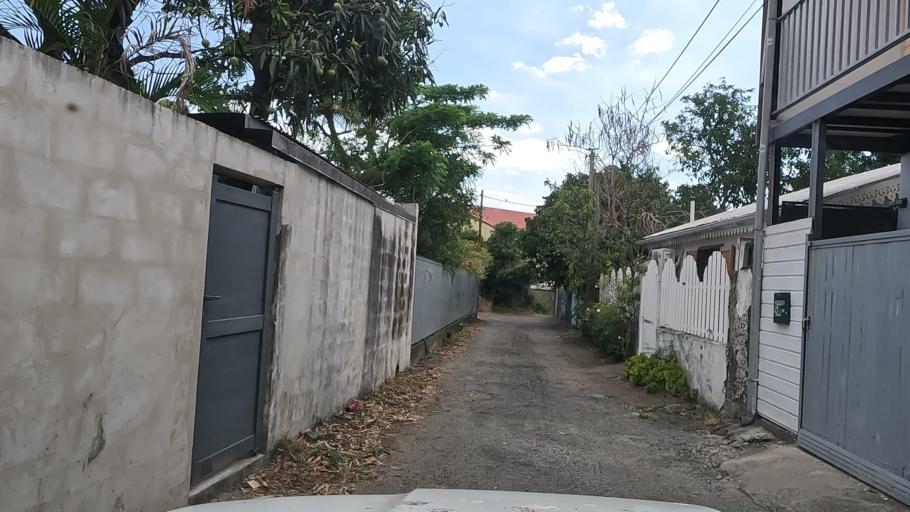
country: RE
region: Reunion
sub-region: Reunion
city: Saint-Louis
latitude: -21.2869
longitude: 55.4137
